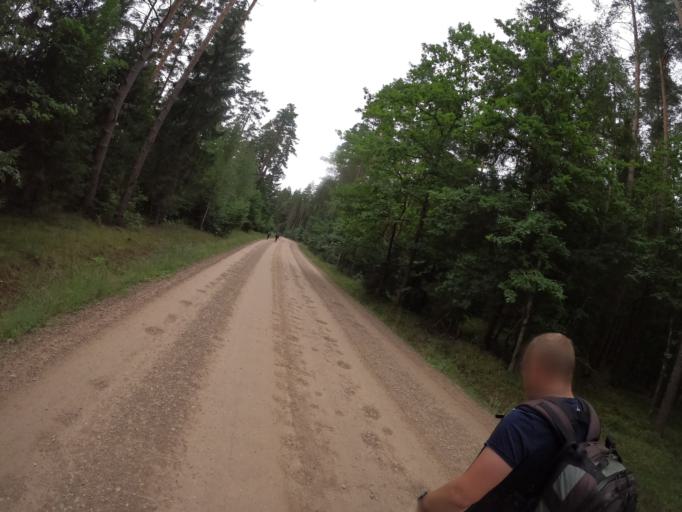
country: LV
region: Kuldigas Rajons
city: Kuldiga
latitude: 57.0009
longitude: 21.9800
